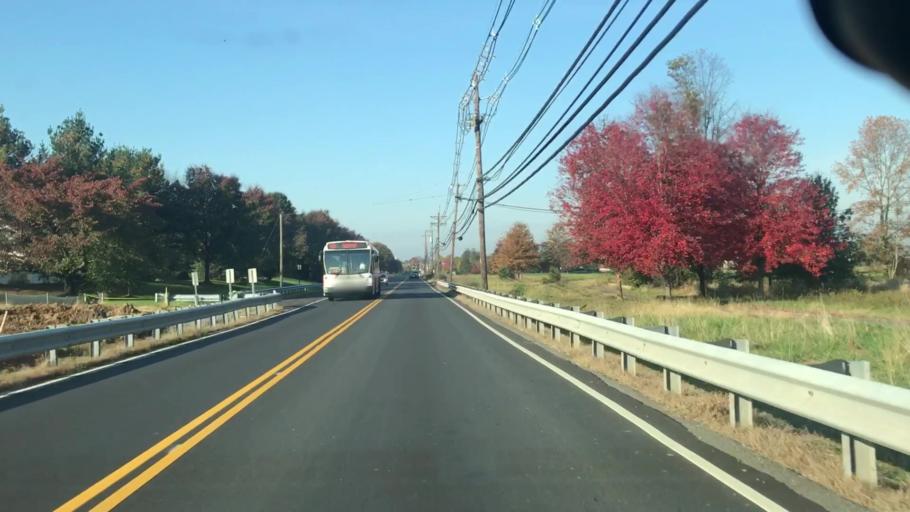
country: US
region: New Jersey
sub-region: Middlesex County
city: Princeton Meadows
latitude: 40.3360
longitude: -74.5773
